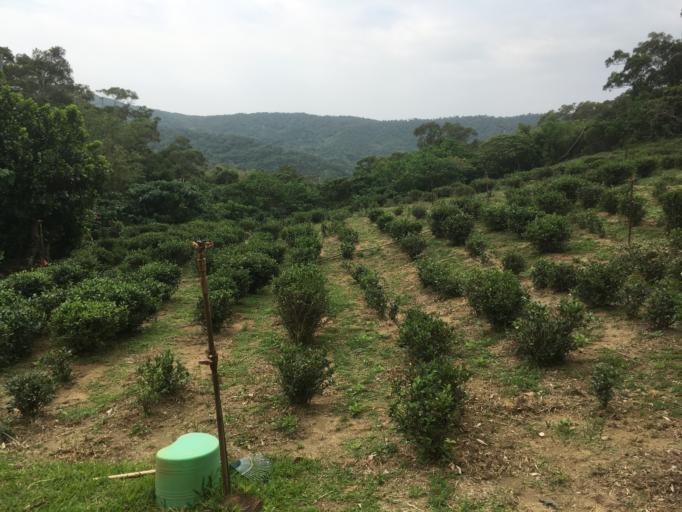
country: TW
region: Taiwan
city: Hengchun
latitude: 21.9947
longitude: 120.8236
